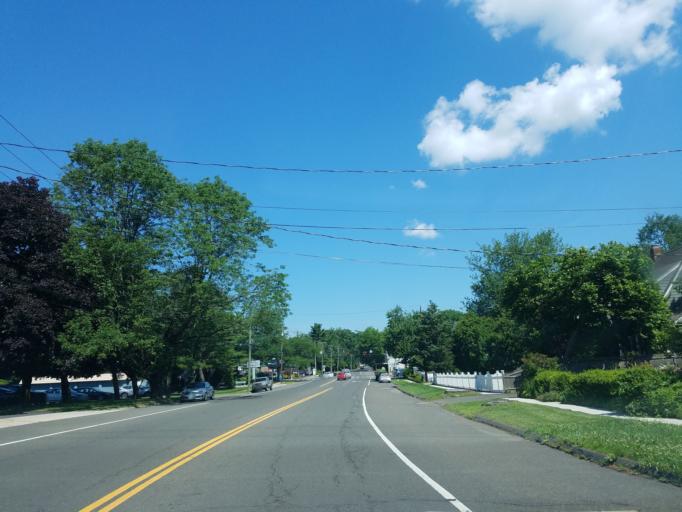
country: US
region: Connecticut
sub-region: Fairfield County
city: Bridgeport
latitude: 41.1967
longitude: -73.2357
